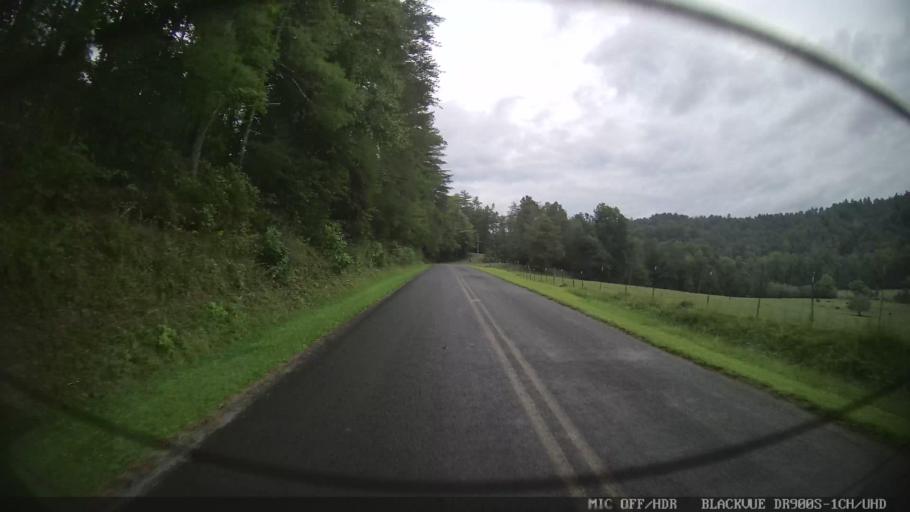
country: US
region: Georgia
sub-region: Gilmer County
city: Ellijay
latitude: 34.7989
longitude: -84.5615
